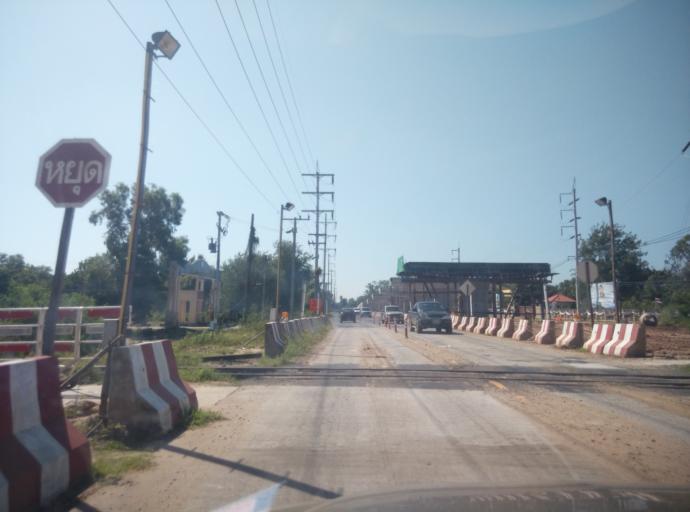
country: TH
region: Sisaket
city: Si Sa Ket
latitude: 15.1214
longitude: 104.2846
